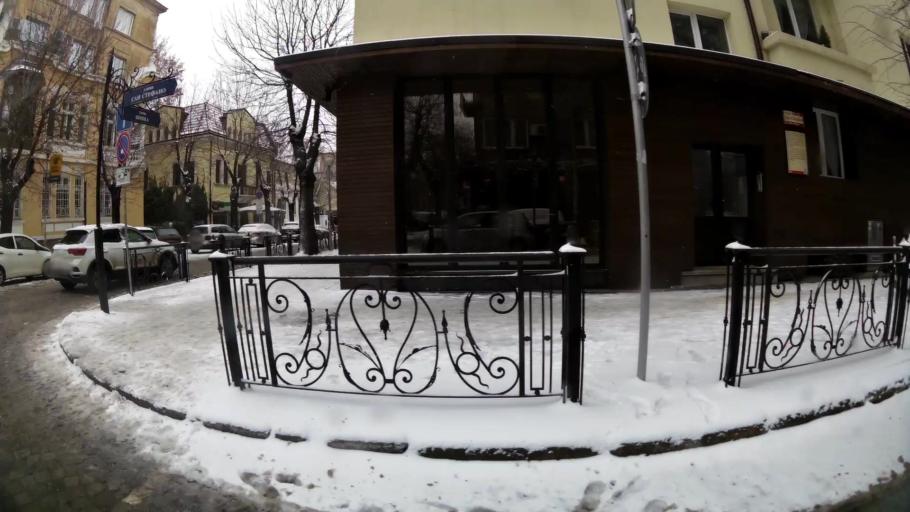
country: BG
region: Sofia-Capital
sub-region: Stolichna Obshtina
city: Sofia
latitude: 42.6940
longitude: 23.3394
